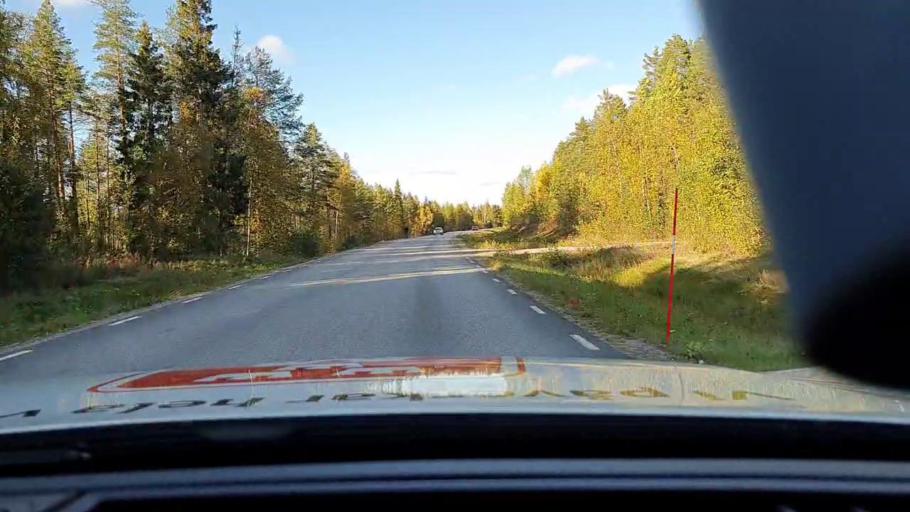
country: SE
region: Norrbotten
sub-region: Pitea Kommun
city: Norrfjarden
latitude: 65.4991
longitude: 21.4757
